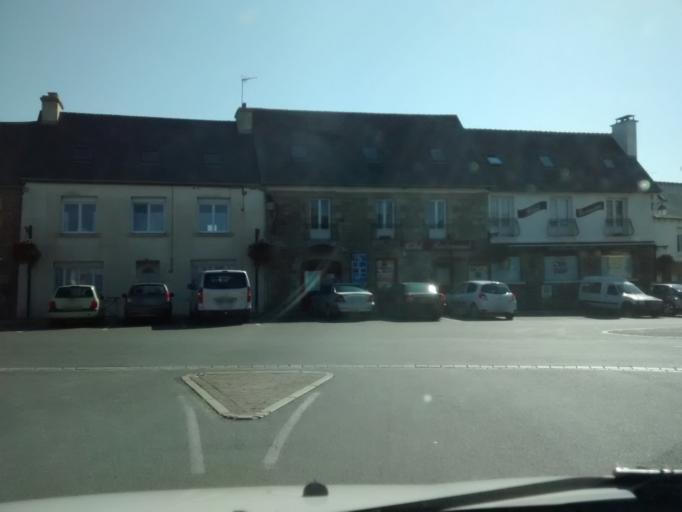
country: FR
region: Brittany
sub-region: Departement des Cotes-d'Armor
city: Pleubian
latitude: 48.8420
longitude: -3.1390
